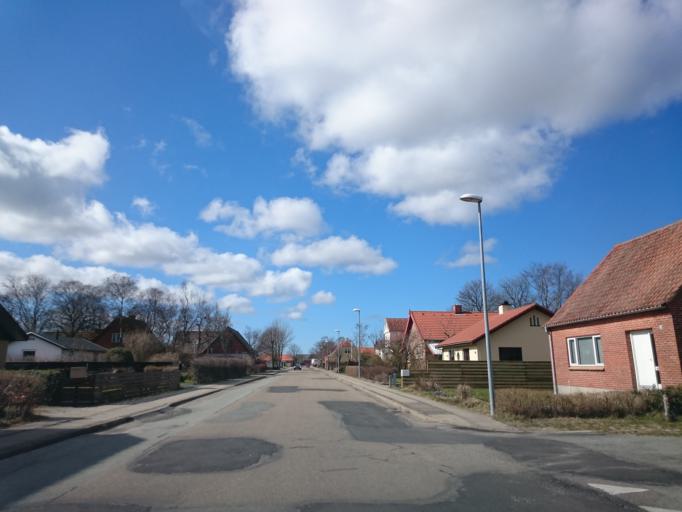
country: DK
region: North Denmark
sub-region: Frederikshavn Kommune
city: Strandby
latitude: 57.5928
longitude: 10.4164
